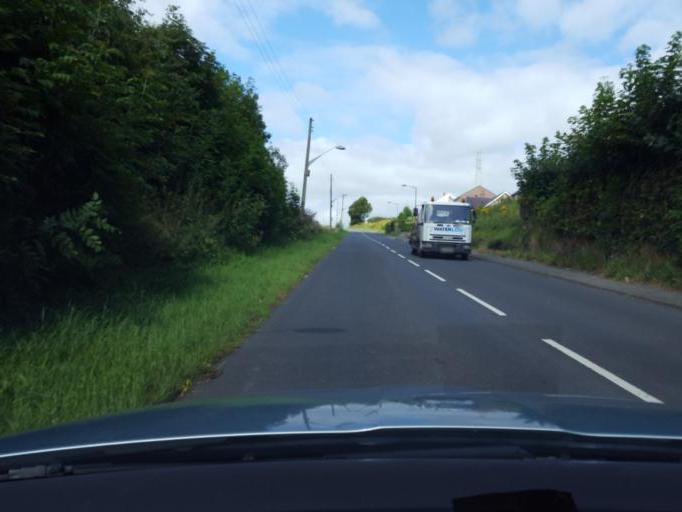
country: GB
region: Wales
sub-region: Denbighshire
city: Corwen
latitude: 52.9869
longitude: -3.3702
